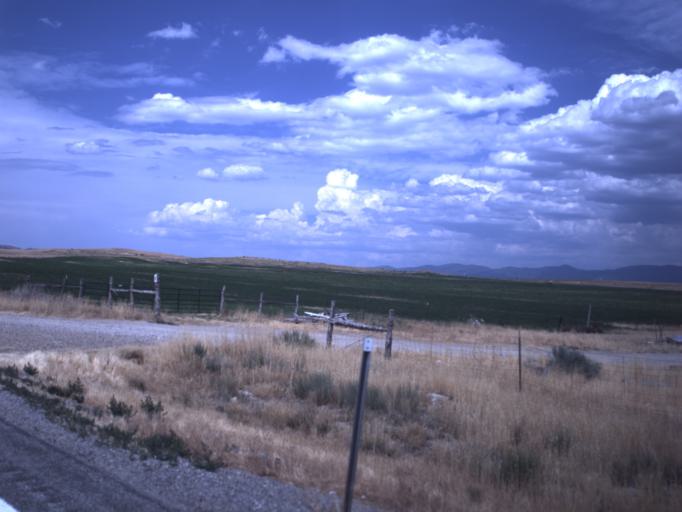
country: US
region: Utah
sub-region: Sanpete County
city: Moroni
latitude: 39.4942
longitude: -111.5632
